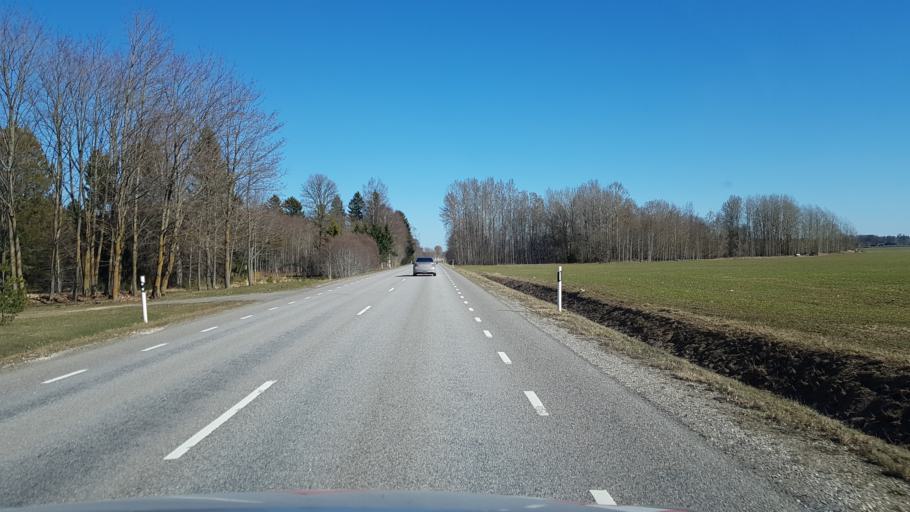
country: EE
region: Laeaene-Virumaa
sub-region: Viru-Nigula vald
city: Kunda
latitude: 59.3565
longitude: 26.6524
